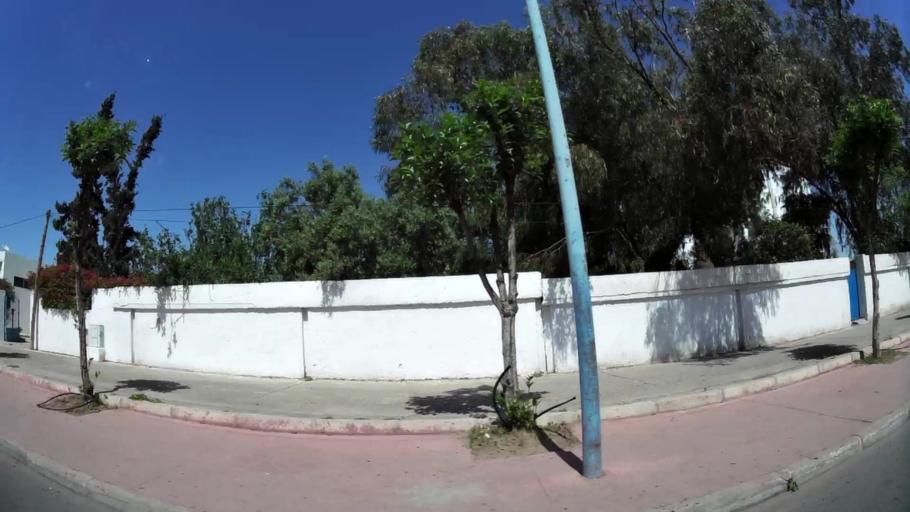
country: MA
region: Souss-Massa-Draa
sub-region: Agadir-Ida-ou-Tnan
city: Agadir
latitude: 30.4109
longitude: -9.5829
